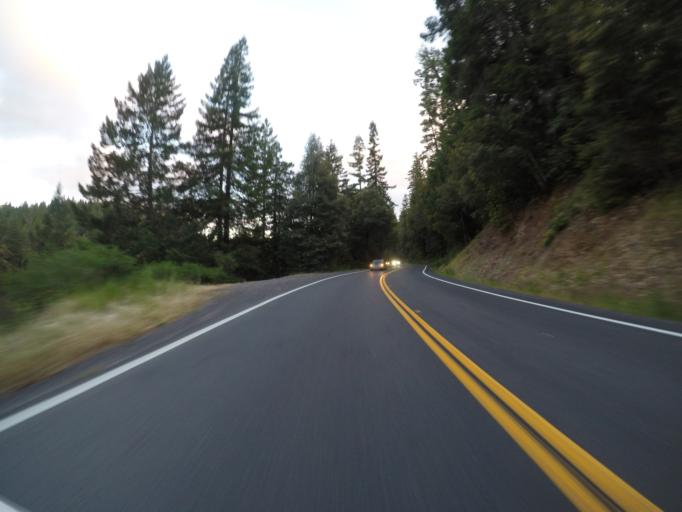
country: US
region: California
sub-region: Humboldt County
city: Redway
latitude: 40.0328
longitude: -123.7932
